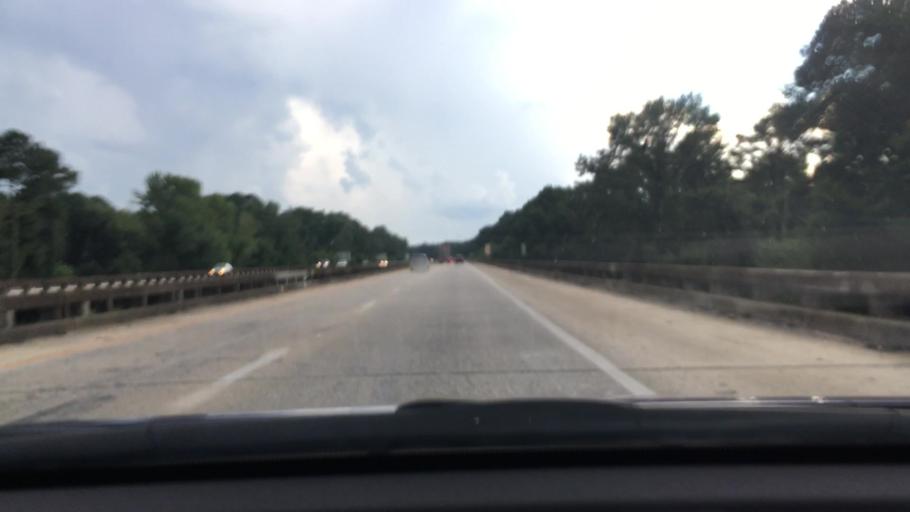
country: US
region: South Carolina
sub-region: Kershaw County
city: Camden
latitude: 34.2185
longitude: -80.6061
